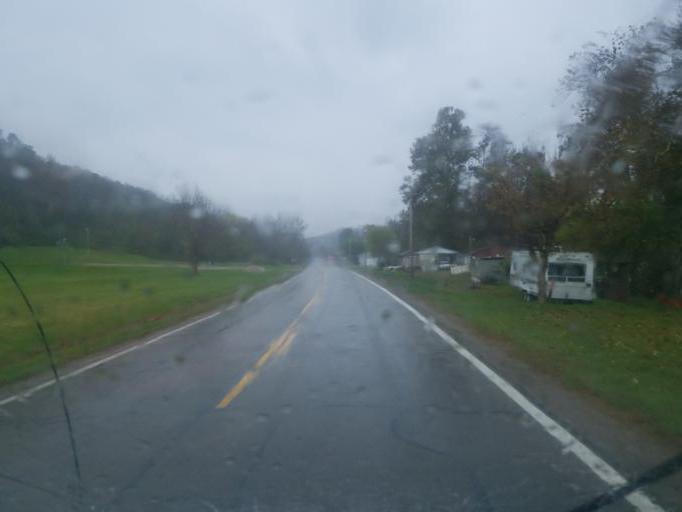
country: US
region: Ohio
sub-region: Muskingum County
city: South Zanesville
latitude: 39.8101
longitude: -81.8909
